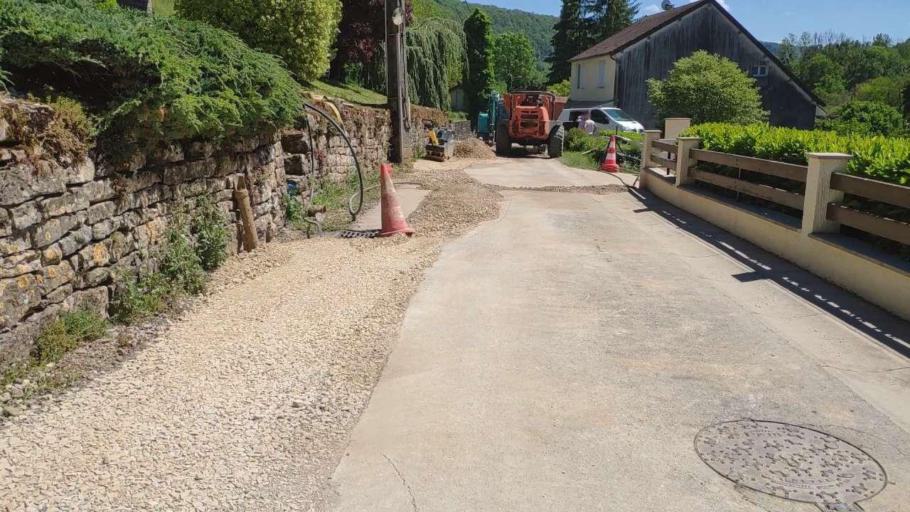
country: FR
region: Franche-Comte
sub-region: Departement du Jura
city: Perrigny
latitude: 46.7406
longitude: 5.6328
